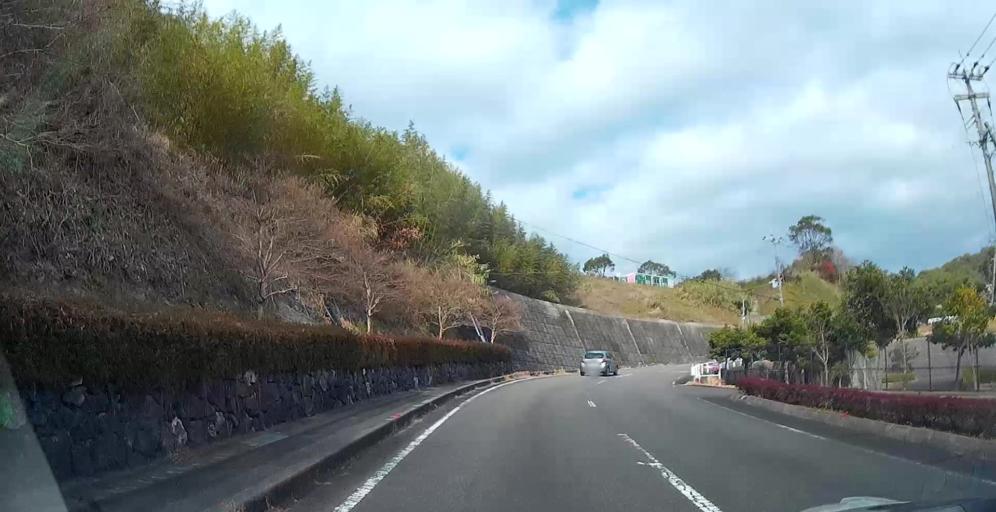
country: JP
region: Kumamoto
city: Minamata
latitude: 32.3202
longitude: 130.4705
